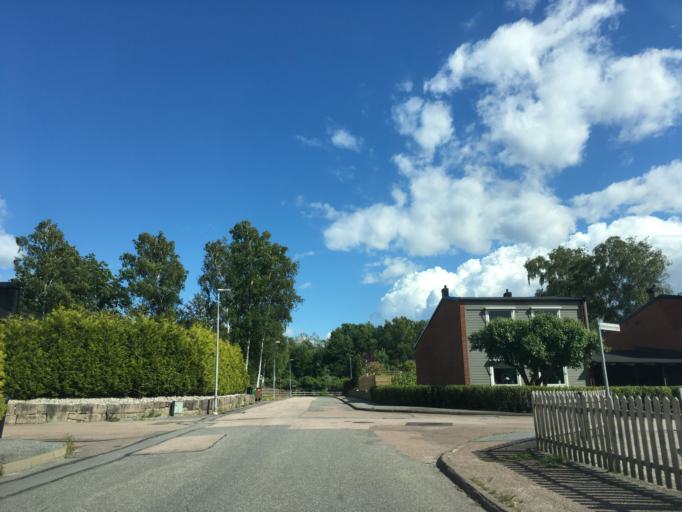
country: SE
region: Vaestra Goetaland
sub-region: Kungalvs Kommun
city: Kungalv
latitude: 57.8694
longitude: 11.9283
